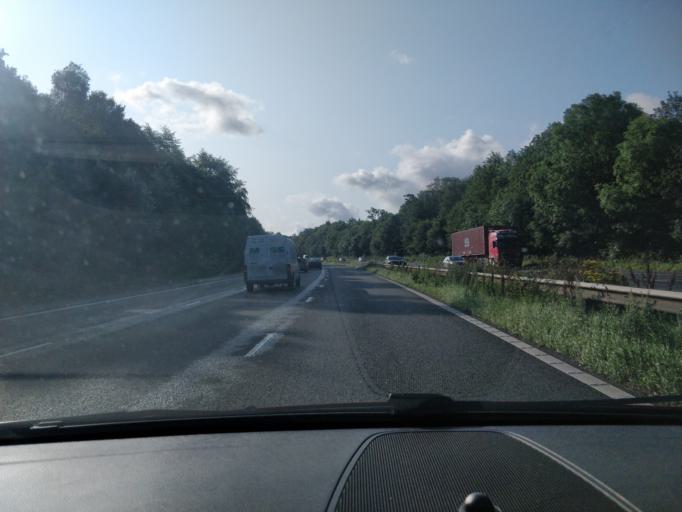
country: GB
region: England
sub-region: Knowsley
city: Knowsley
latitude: 53.4326
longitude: -2.8502
